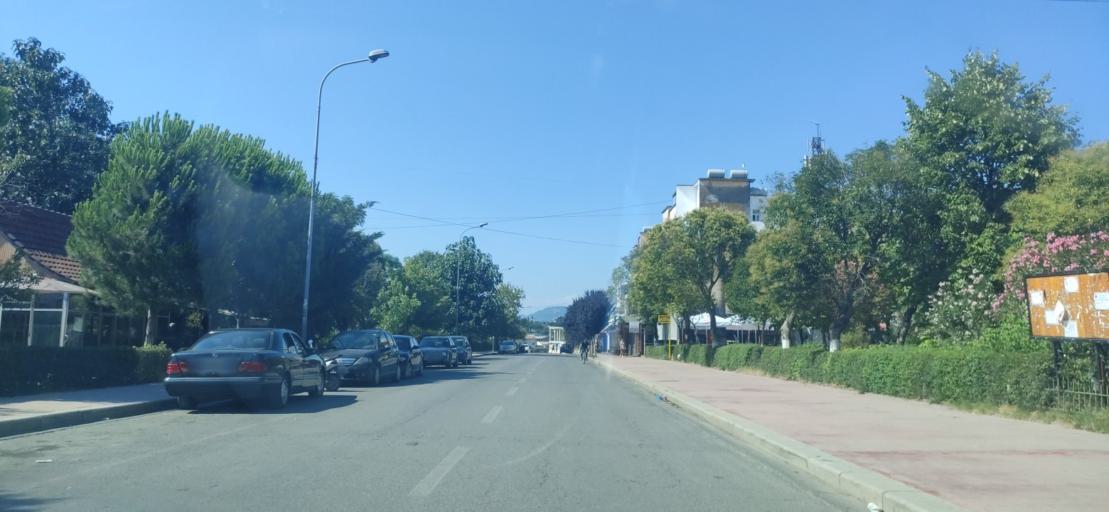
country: AL
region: Lezhe
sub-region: Rrethi i Kurbinit
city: Lac
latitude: 41.6364
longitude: 19.7120
